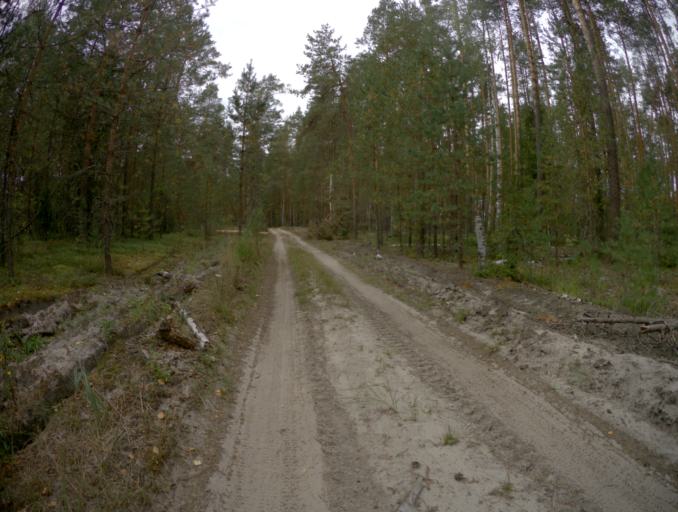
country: RU
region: Vladimir
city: Ivanishchi
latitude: 55.8550
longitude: 40.3665
